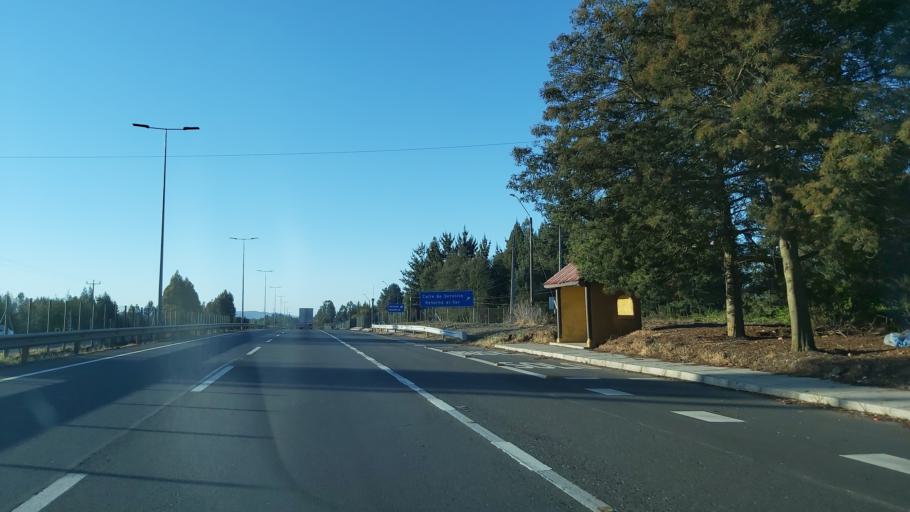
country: CL
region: Araucania
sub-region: Provincia de Malleco
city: Victoria
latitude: -38.0864
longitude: -72.3633
